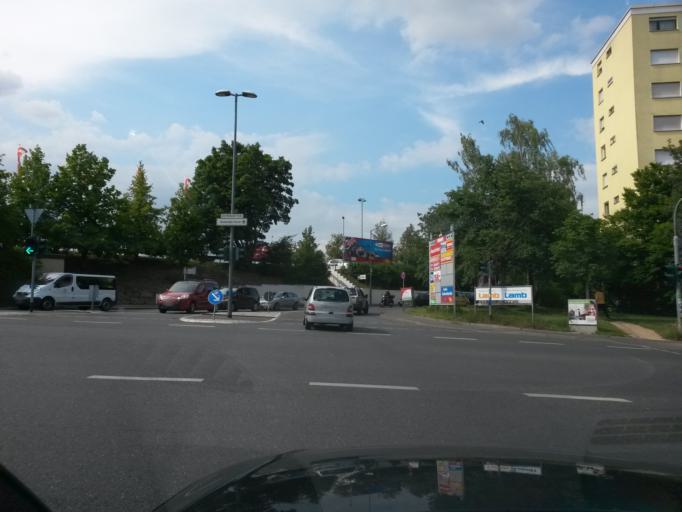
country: DE
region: Bavaria
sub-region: Regierungsbezirk Unterfranken
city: Wuerzburg
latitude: 49.8109
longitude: 9.9779
